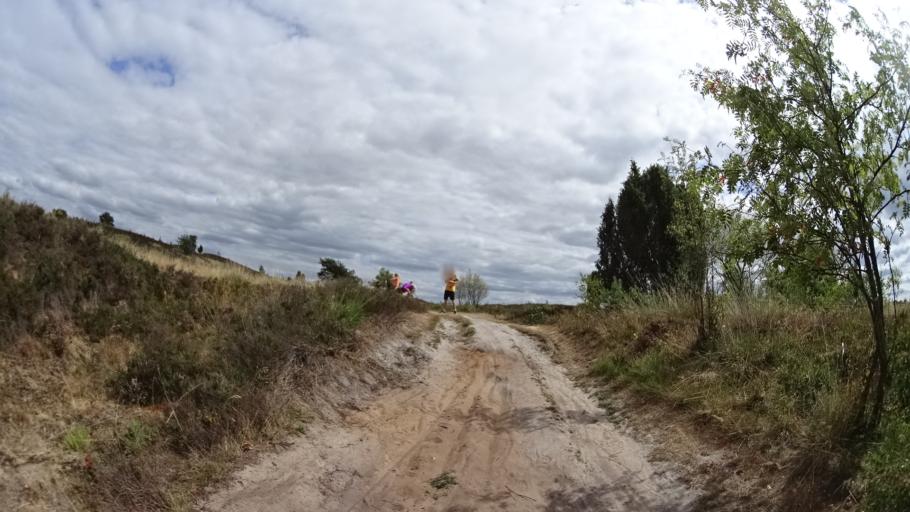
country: DE
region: Lower Saxony
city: Undeloh
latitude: 53.1863
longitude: 9.9924
